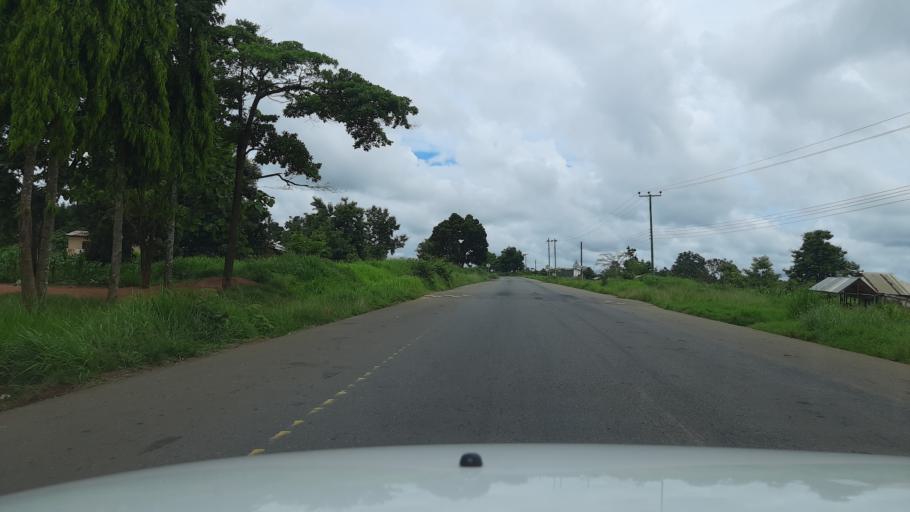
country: TZ
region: Tanga
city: Chanika
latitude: -5.9052
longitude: 38.2404
